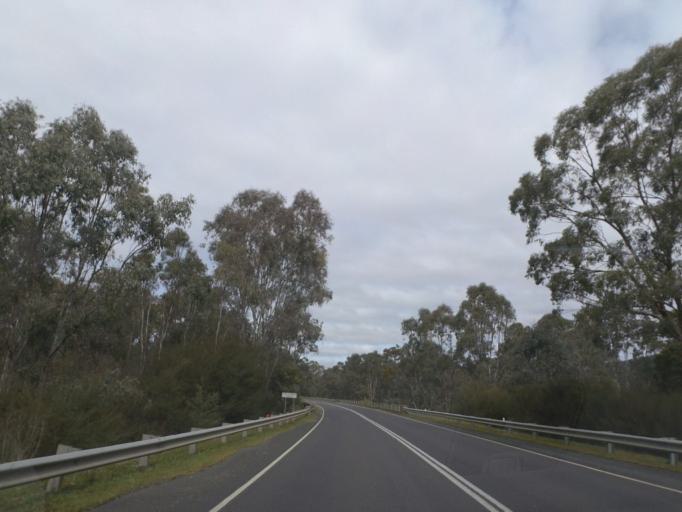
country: AU
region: Victoria
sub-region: Murrindindi
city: Kinglake West
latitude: -37.1451
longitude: 145.2671
